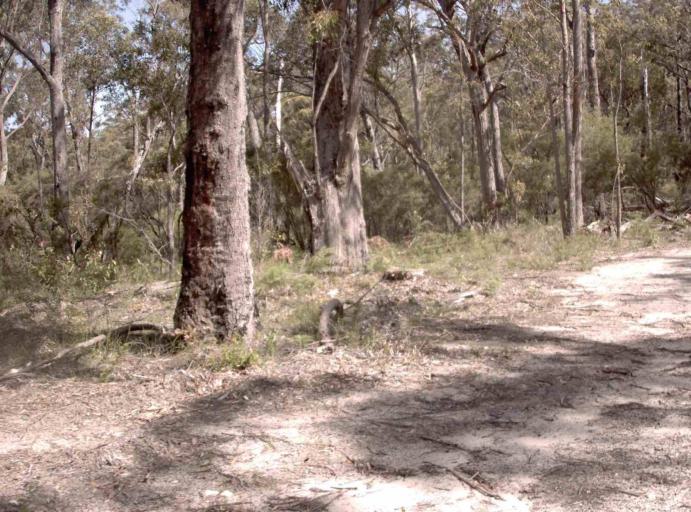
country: AU
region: New South Wales
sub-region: Bega Valley
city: Eden
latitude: -37.5377
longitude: 149.6969
